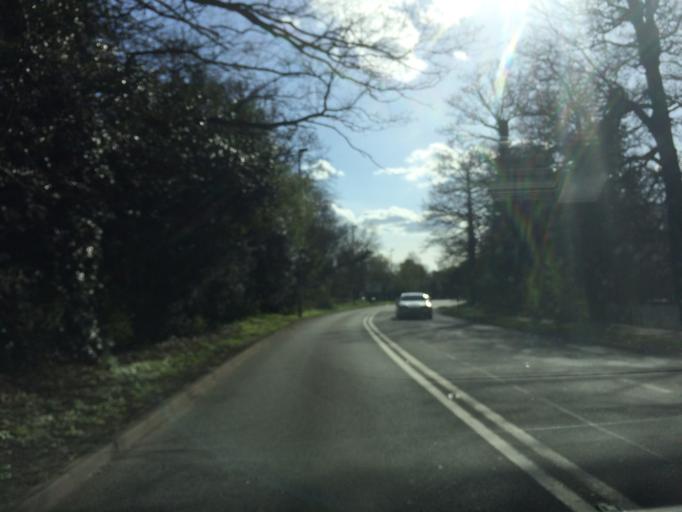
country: GB
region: England
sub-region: Surrey
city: Ottershaw
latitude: 51.3667
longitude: -0.5309
